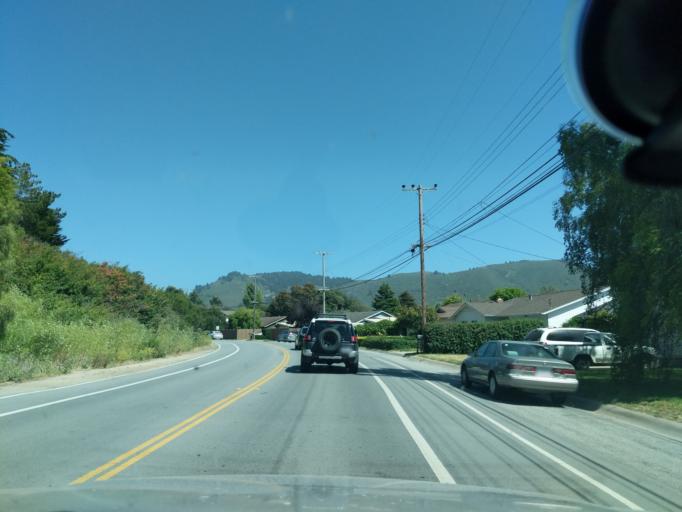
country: US
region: California
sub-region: Monterey County
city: Carmel-by-the-Sea
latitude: 36.5410
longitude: -121.9156
